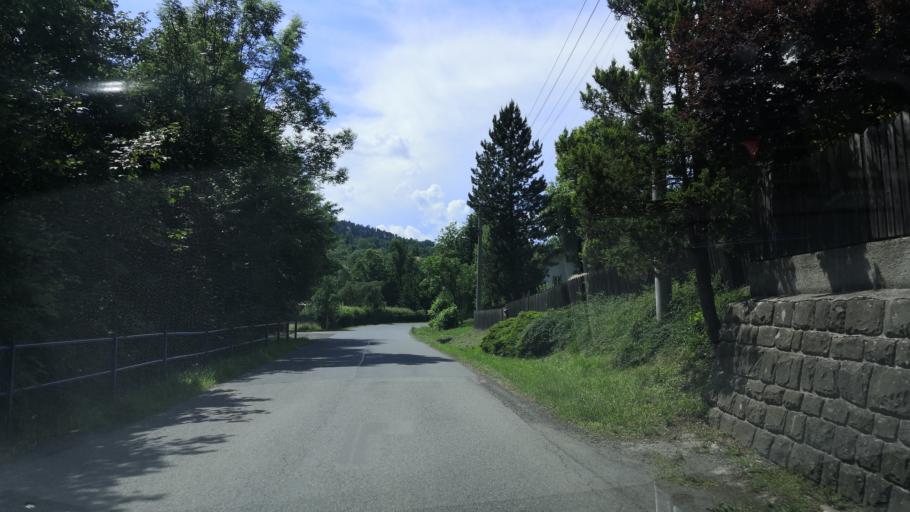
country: CZ
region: Zlin
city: Vidce
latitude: 49.4430
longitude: 18.0878
